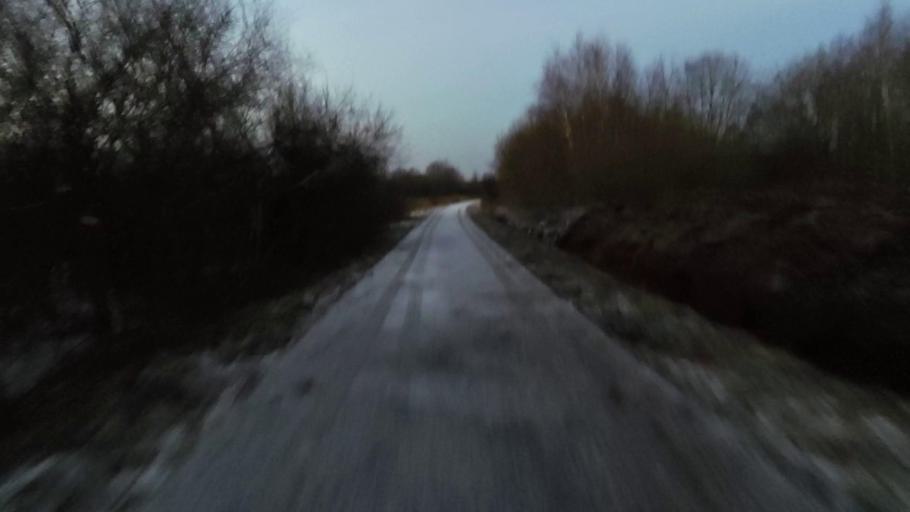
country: PL
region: West Pomeranian Voivodeship
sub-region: Powiat swidwinski
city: Polczyn-Zdroj
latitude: 53.7661
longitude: 16.0692
